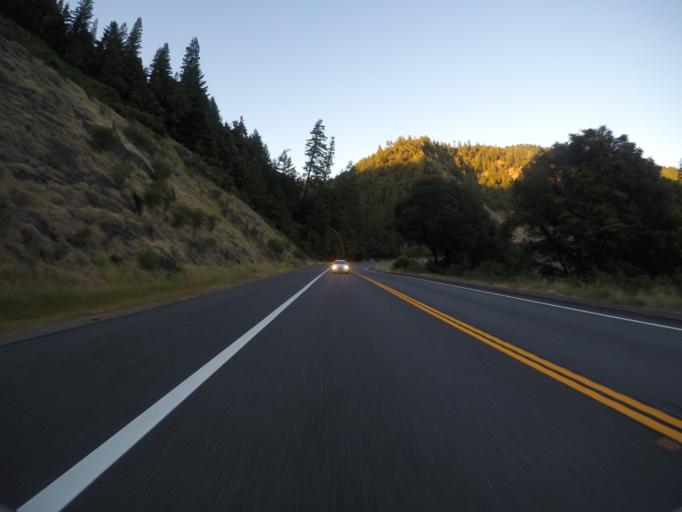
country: US
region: California
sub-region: Humboldt County
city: Redway
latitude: 39.9070
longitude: -123.7556
